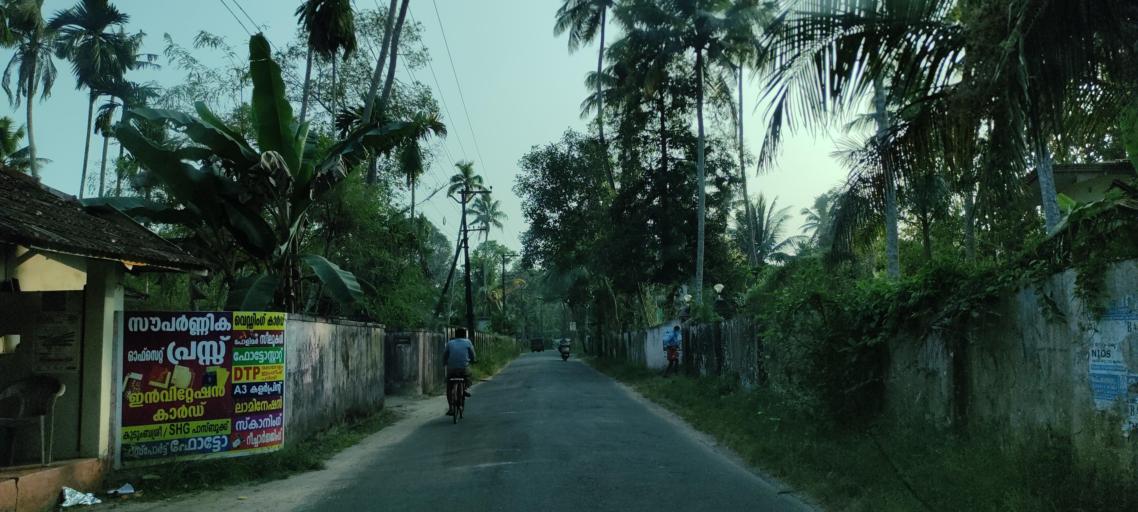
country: IN
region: Kerala
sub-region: Alappuzha
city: Shertallai
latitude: 9.6686
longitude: 76.3539
